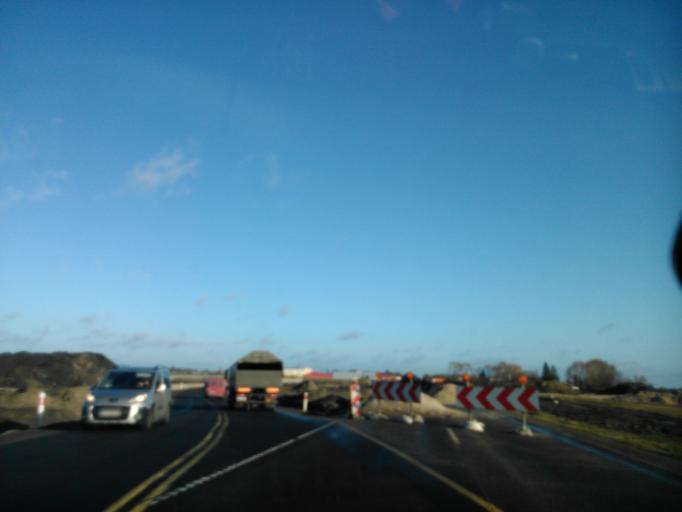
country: PL
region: Kujawsko-Pomorskie
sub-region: Powiat inowroclawski
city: Inowroclaw
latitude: 52.8179
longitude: 18.2931
